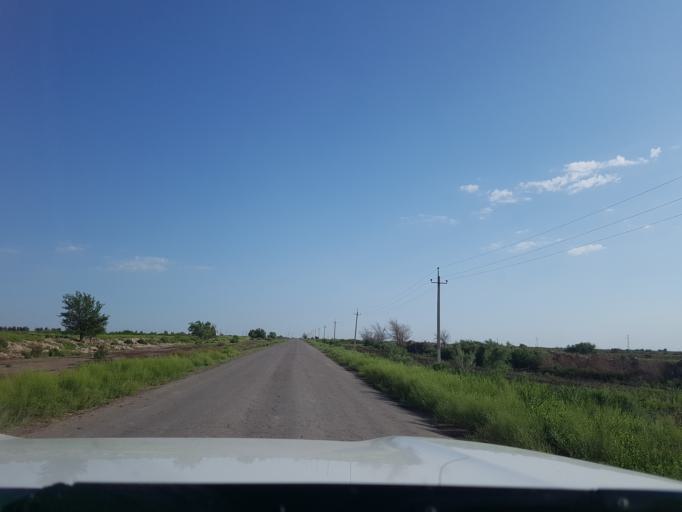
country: TM
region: Dasoguz
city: Koeneuergench
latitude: 41.8568
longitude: 58.7052
